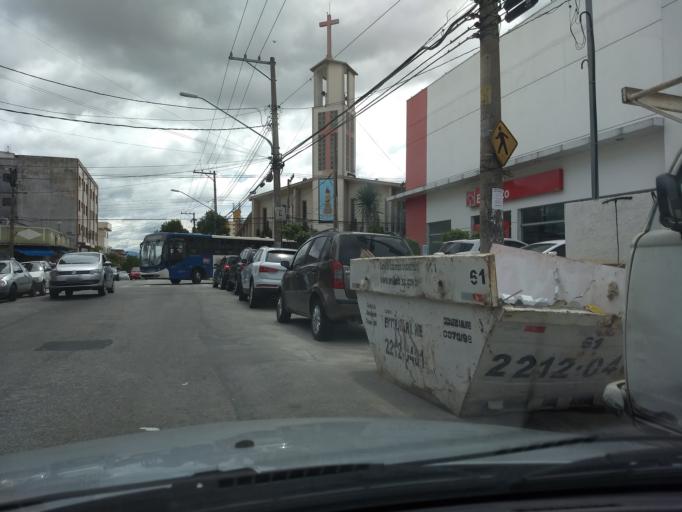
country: BR
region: Sao Paulo
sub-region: Guarulhos
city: Guarulhos
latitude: -23.4882
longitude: -46.5833
